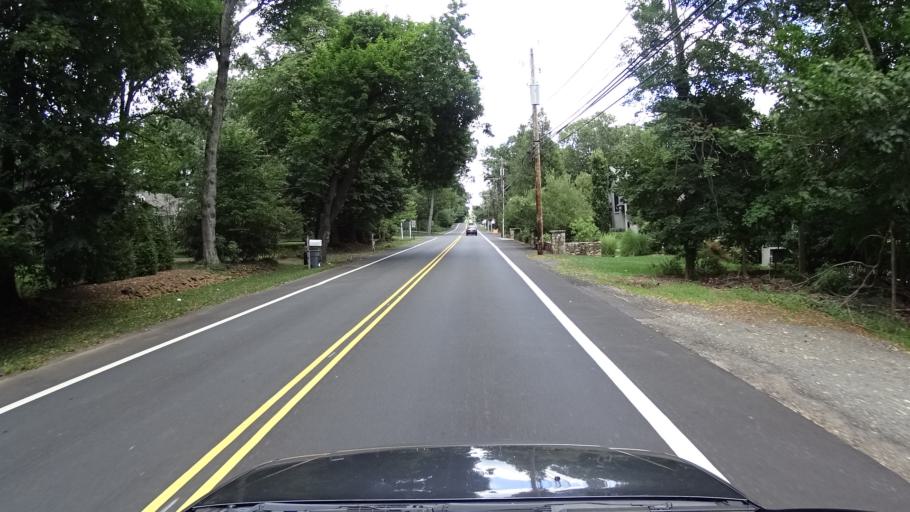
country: US
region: New Jersey
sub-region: Morris County
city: Chatham
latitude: 40.7253
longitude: -74.3978
